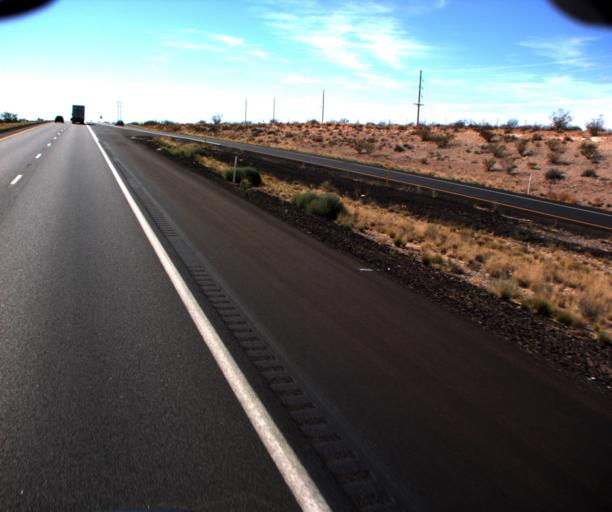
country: US
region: Arizona
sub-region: Mohave County
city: Beaver Dam
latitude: 36.8897
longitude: -113.9332
